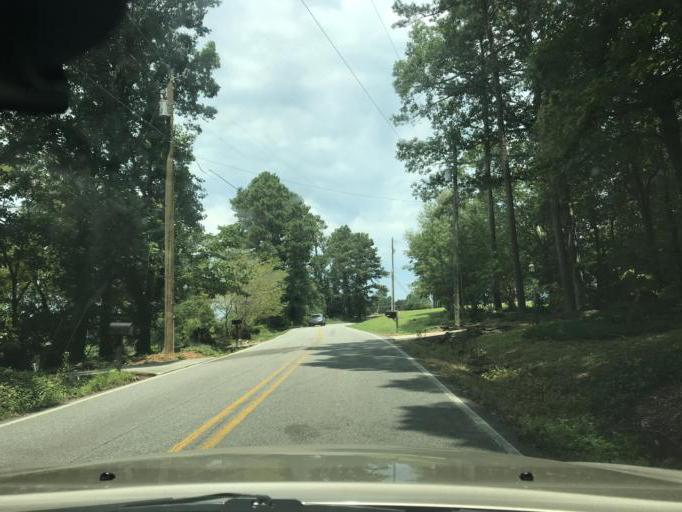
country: US
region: Georgia
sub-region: Forsyth County
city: Cumming
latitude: 34.2916
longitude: -84.2156
